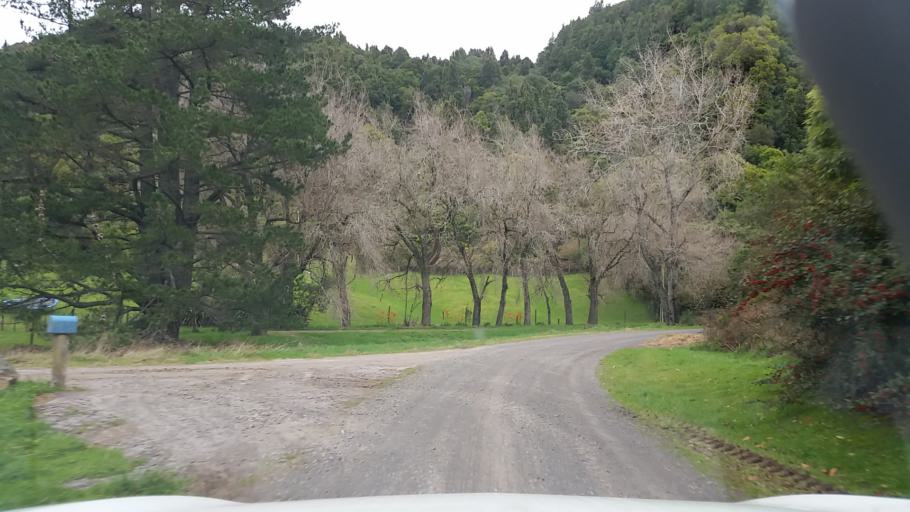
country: NZ
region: Bay of Plenty
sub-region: Rotorua District
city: Rotorua
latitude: -38.1591
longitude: 176.3691
